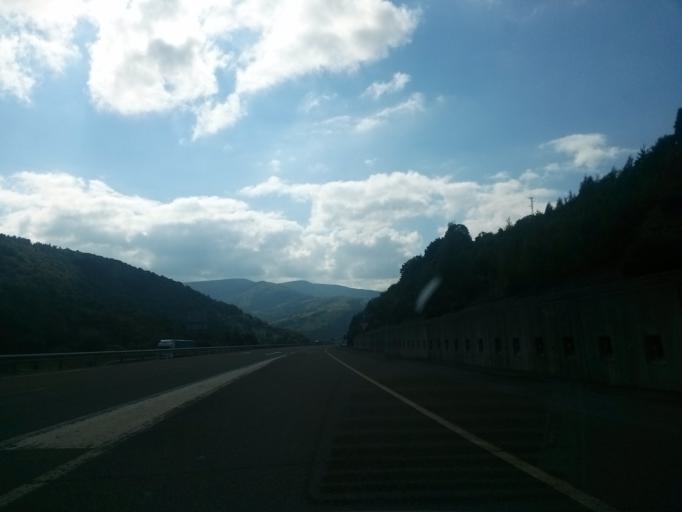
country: ES
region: Castille and Leon
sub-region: Provincia de Leon
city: Balboa
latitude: 42.7270
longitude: -7.0333
